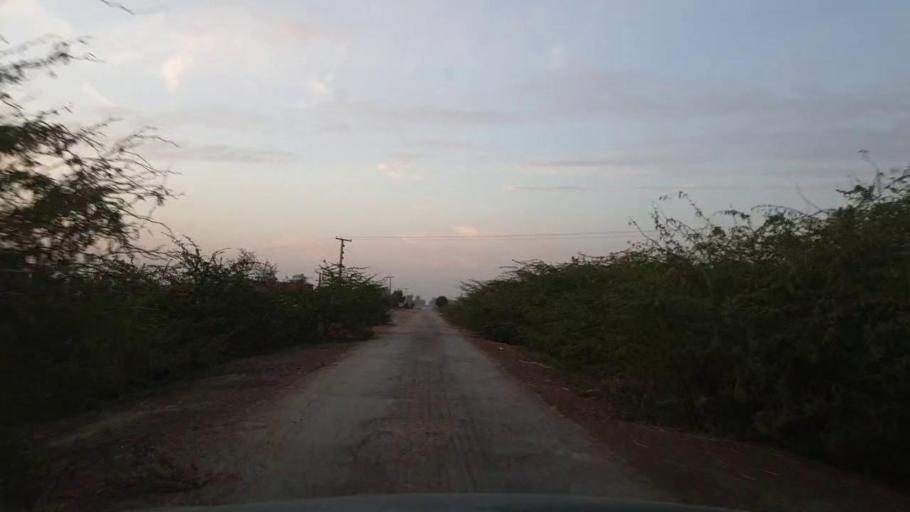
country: PK
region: Sindh
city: Kunri
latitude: 25.1386
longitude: 69.5615
